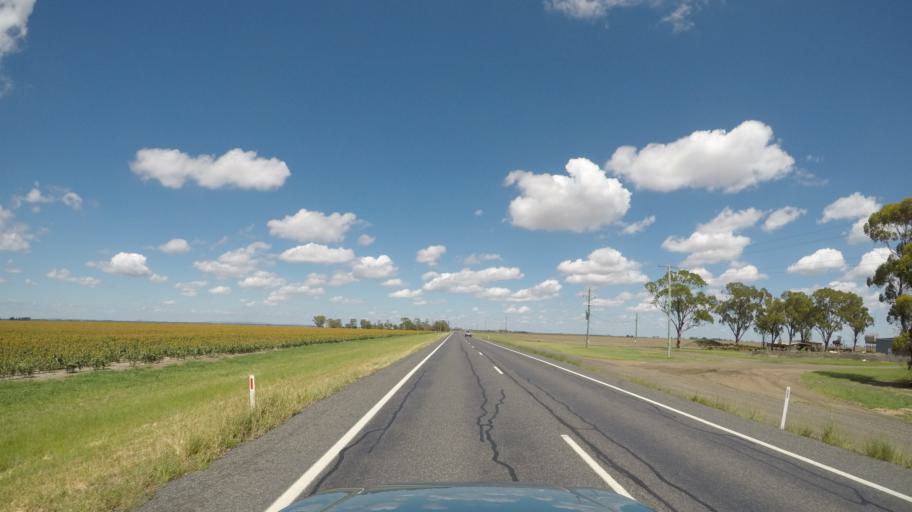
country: AU
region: Queensland
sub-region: Toowoomba
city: Oakey
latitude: -27.7575
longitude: 151.4925
